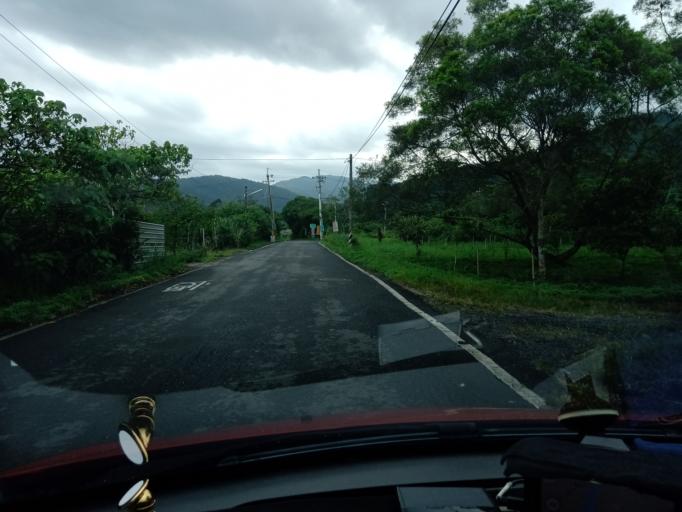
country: TW
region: Taiwan
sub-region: Yilan
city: Yilan
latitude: 24.7815
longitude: 121.7180
